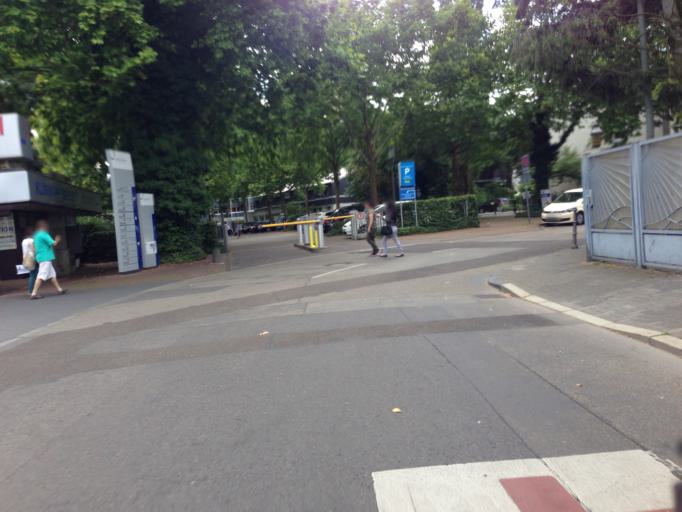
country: DE
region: Hesse
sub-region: Regierungsbezirk Darmstadt
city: Hanau am Main
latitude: 50.1335
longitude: 8.9223
